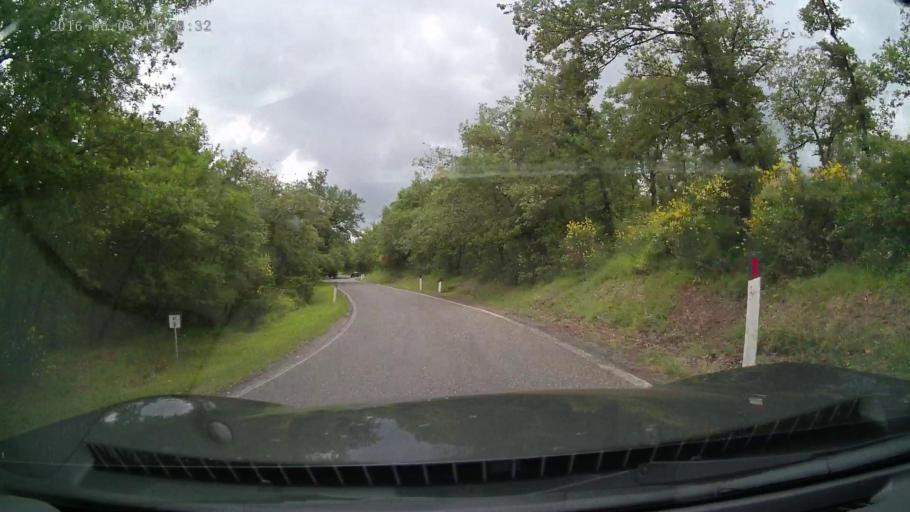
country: IT
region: Tuscany
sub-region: Province of Florence
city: Panzano in Chianti
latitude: 43.5596
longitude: 11.2967
